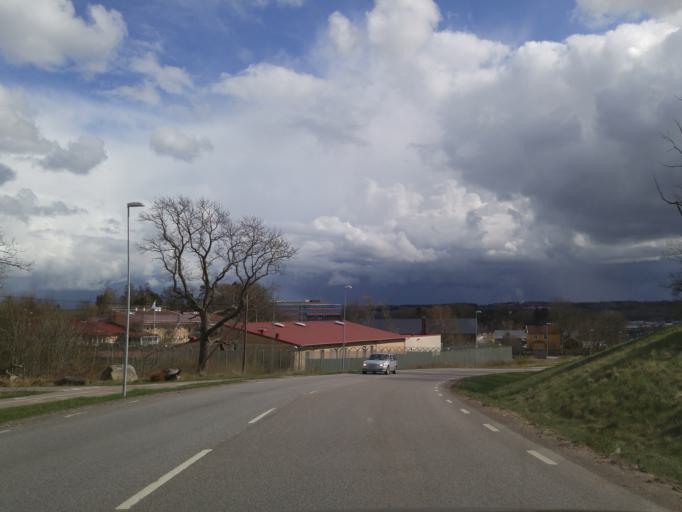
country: SE
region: Vaestra Goetaland
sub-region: Goteborg
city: Majorna
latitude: 57.6555
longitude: 11.9506
